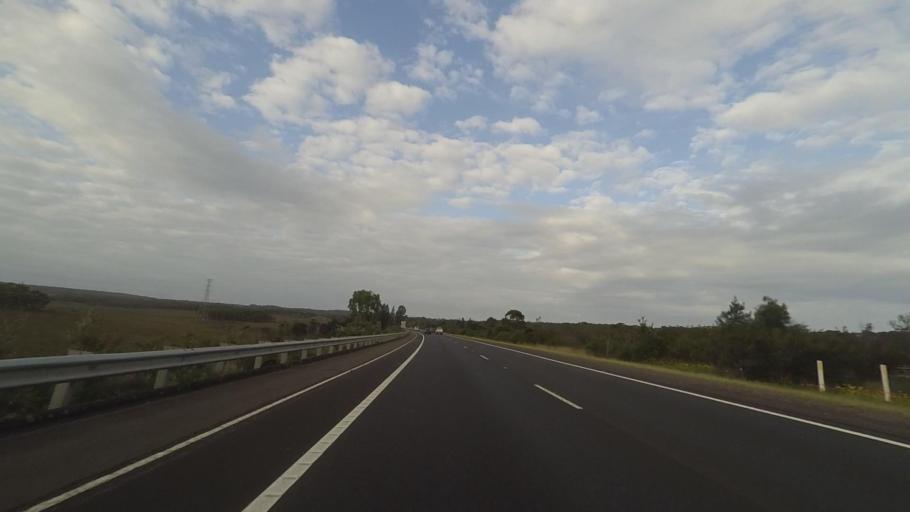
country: AU
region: New South Wales
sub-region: Wollongong
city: Bulli
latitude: -34.2873
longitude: 150.9266
